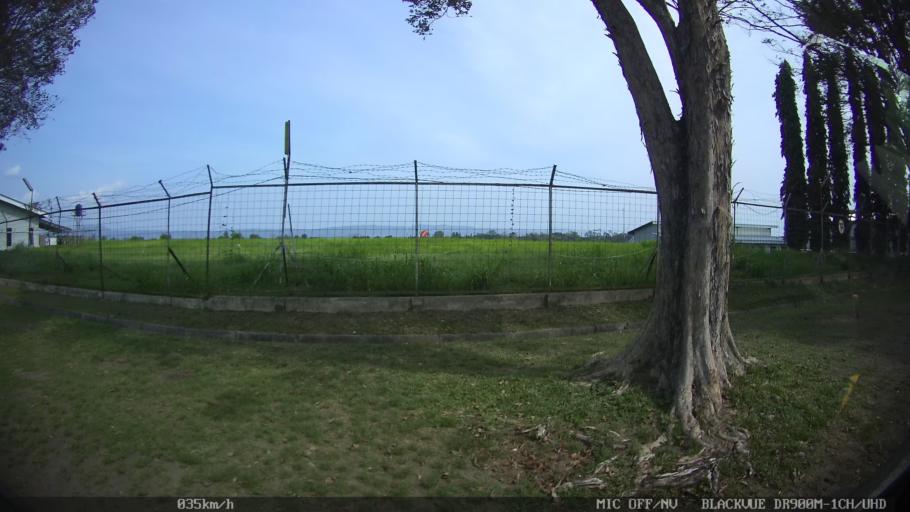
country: ID
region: Daerah Istimewa Yogyakarta
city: Depok
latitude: -7.7851
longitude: 110.4402
